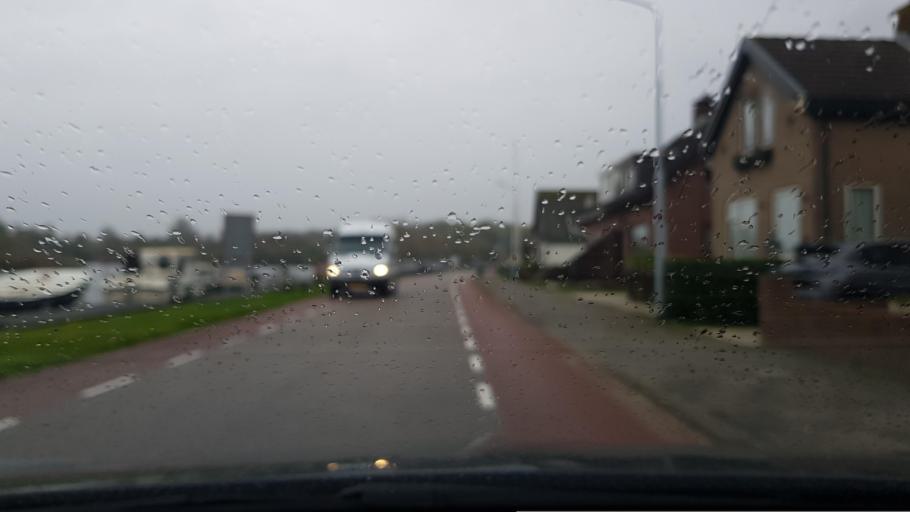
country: NL
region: North Holland
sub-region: Gemeente Amstelveen
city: Amstelveen
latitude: 52.3281
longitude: 4.8141
